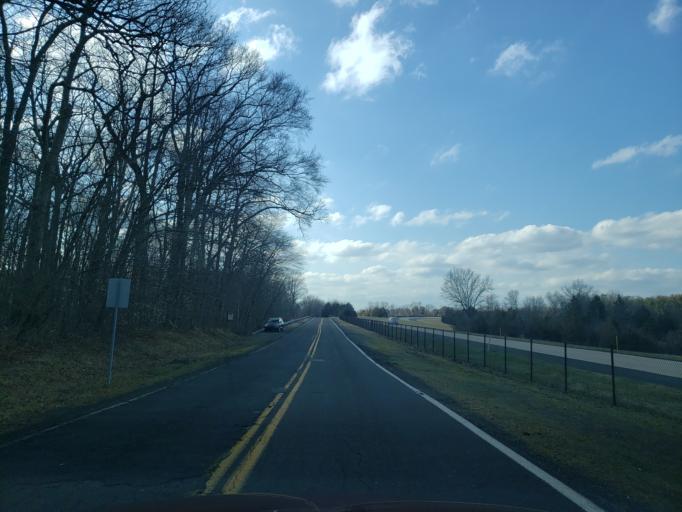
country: US
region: Pennsylvania
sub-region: Bucks County
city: Doylestown
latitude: 40.2913
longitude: -75.1353
